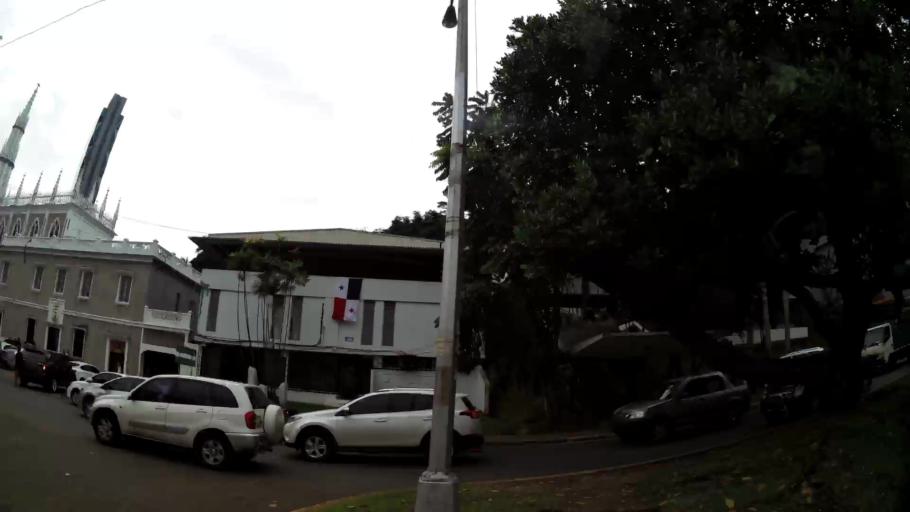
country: PA
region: Panama
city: Panama
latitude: 8.9822
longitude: -79.5285
